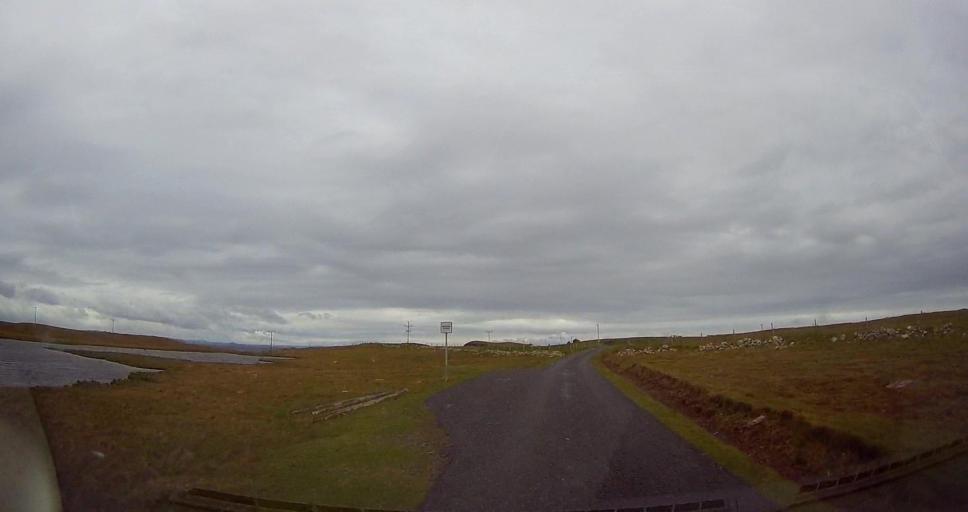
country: GB
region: Scotland
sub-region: Shetland Islands
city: Lerwick
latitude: 60.4844
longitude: -1.6076
